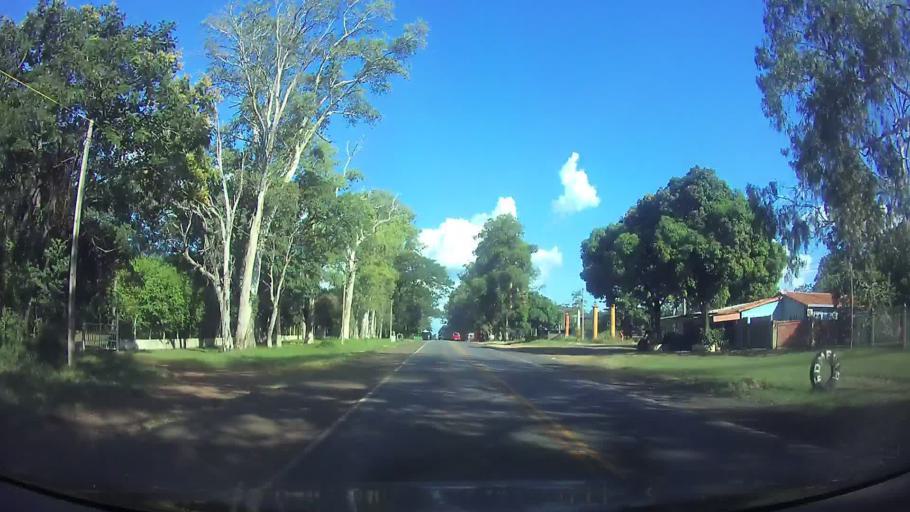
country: PY
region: Cordillera
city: Eusebio Ayala
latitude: -25.4010
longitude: -56.9473
